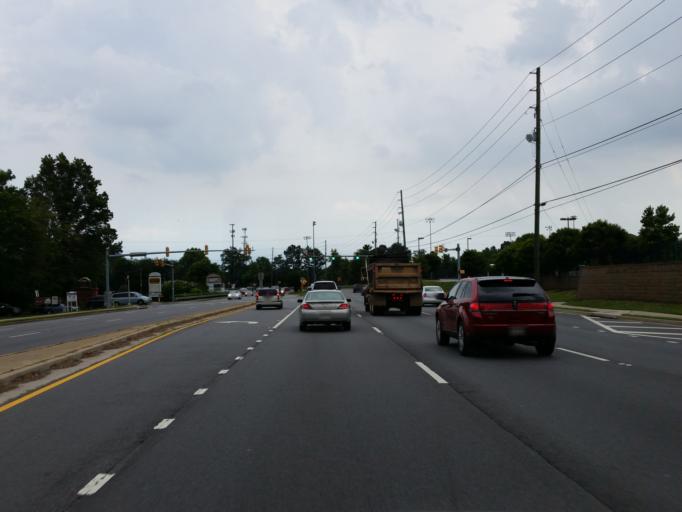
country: US
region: Georgia
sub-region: Fulton County
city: Sandy Springs
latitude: 33.9702
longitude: -84.4135
